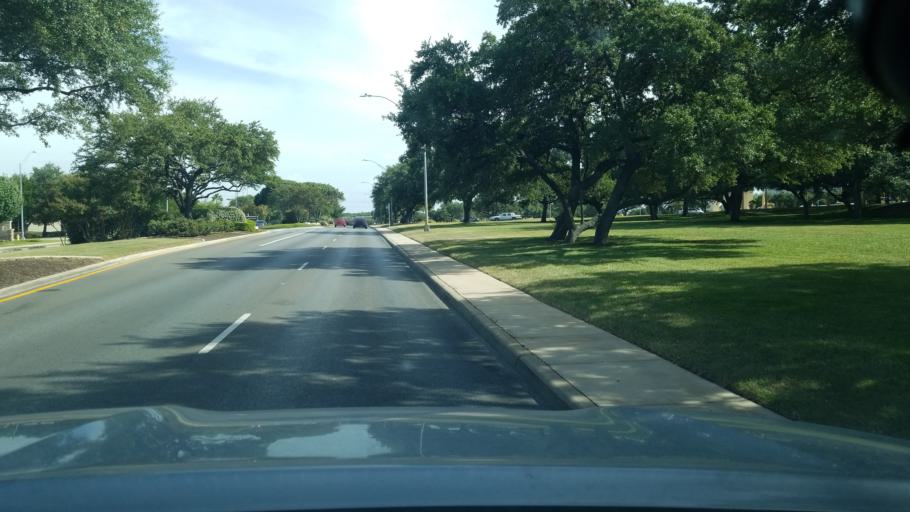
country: US
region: Texas
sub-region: Bexar County
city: Hollywood Park
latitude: 29.6127
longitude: -98.4935
